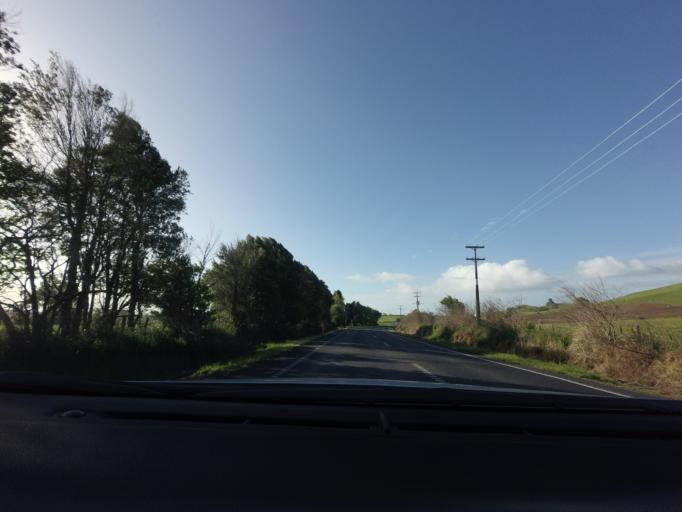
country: NZ
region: Waikato
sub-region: Hauraki District
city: Ngatea
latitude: -37.4534
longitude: 175.5097
